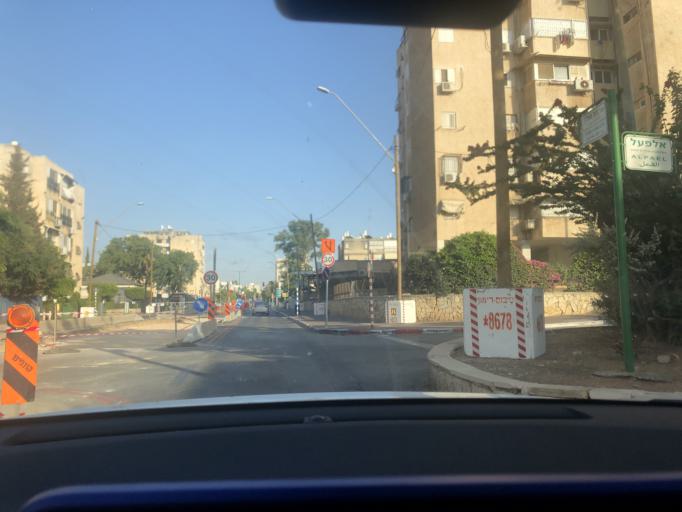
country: IL
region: Central District
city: Lod
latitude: 31.9505
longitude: 34.8868
